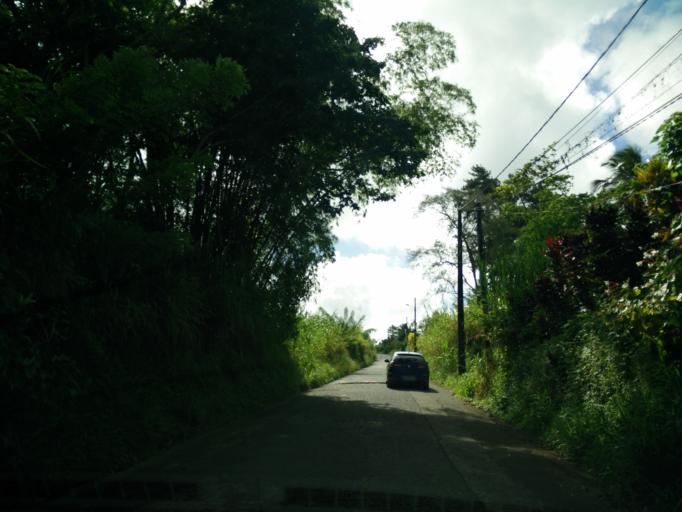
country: MQ
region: Martinique
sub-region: Martinique
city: Basse-Pointe
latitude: 14.8202
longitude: -61.1248
